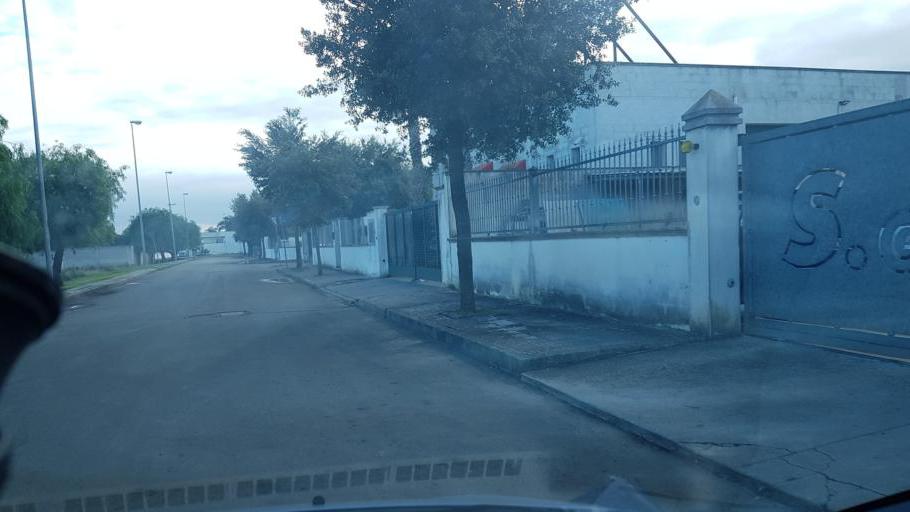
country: IT
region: Apulia
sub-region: Provincia di Lecce
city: Veglie
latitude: 40.3463
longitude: 17.9705
